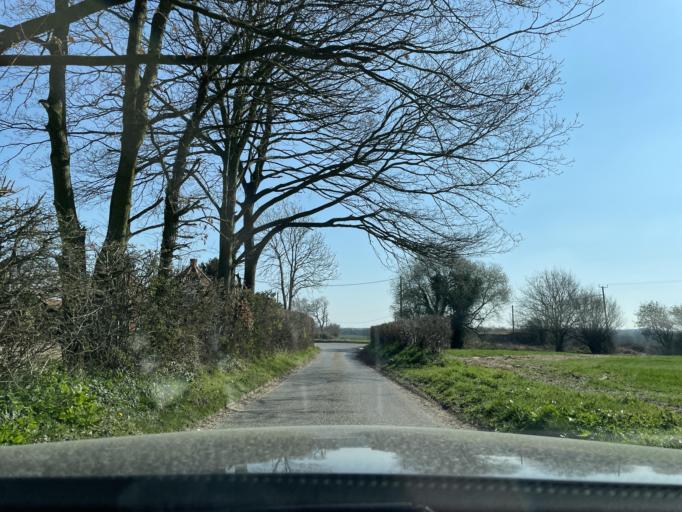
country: GB
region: England
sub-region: Norfolk
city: Hingham
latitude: 52.6170
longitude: 0.9937
